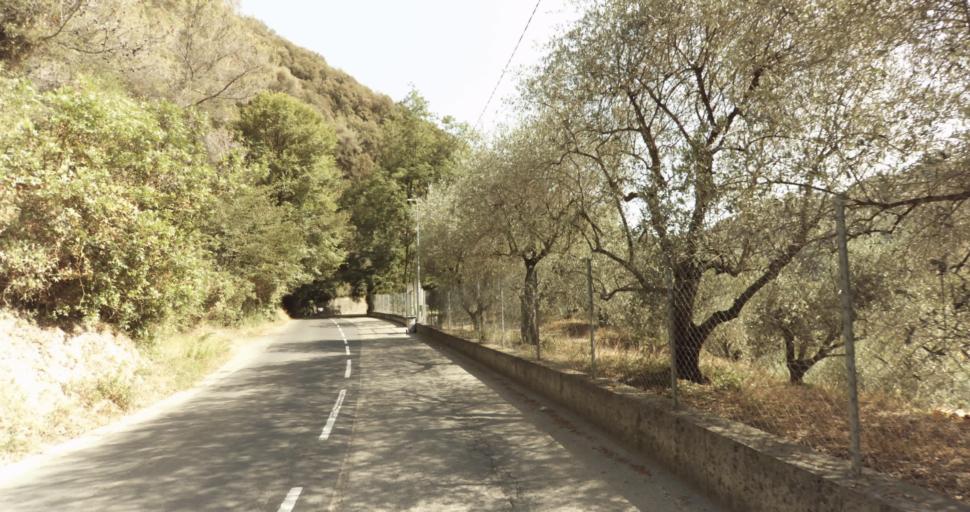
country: FR
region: Provence-Alpes-Cote d'Azur
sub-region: Departement des Alpes-Maritimes
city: Sainte-Agnes
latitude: 43.7952
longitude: 7.4806
